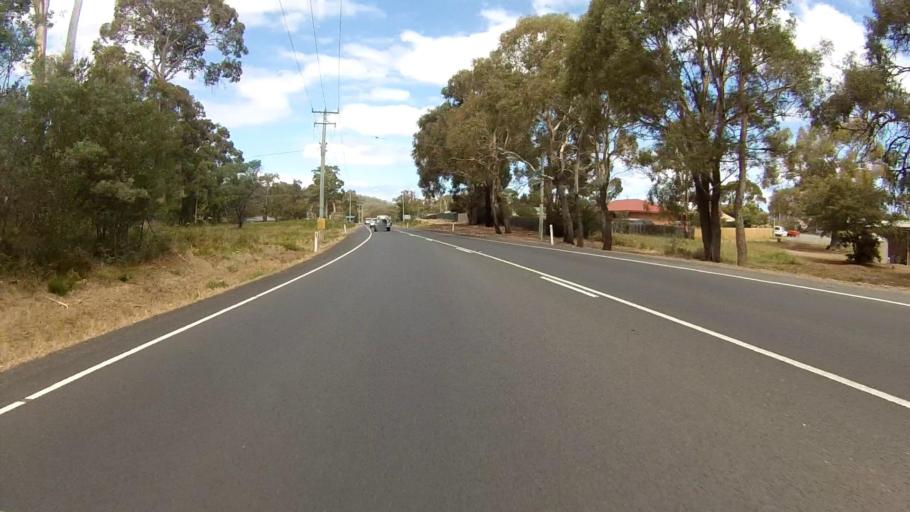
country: AU
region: Tasmania
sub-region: Sorell
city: Sorell
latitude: -42.8421
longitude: 147.6233
